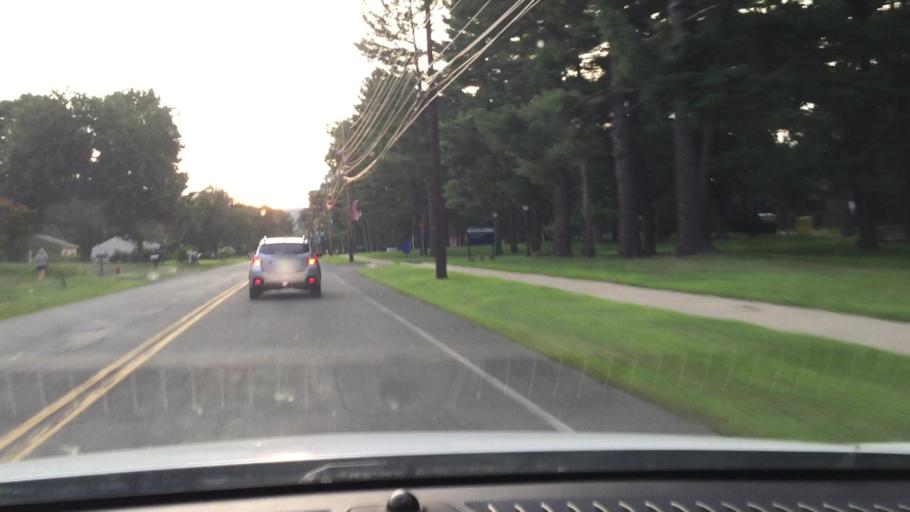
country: US
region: Massachusetts
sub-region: Hampden County
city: Westfield
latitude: 42.1302
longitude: -72.7968
